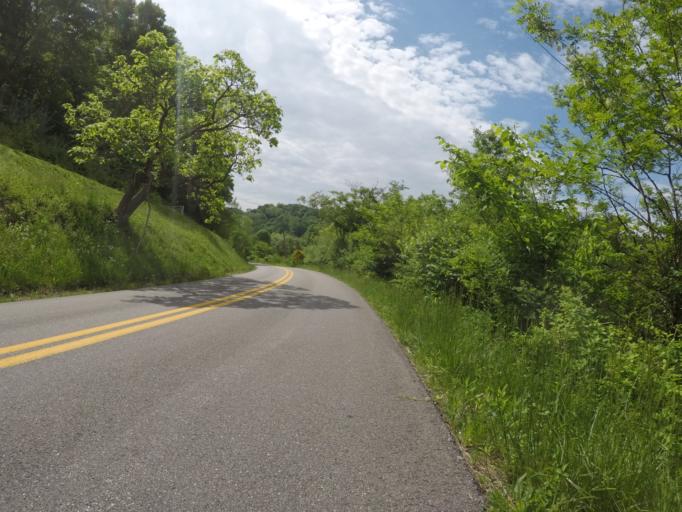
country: US
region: West Virginia
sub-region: Wayne County
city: Ceredo
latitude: 38.3387
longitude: -82.5753
